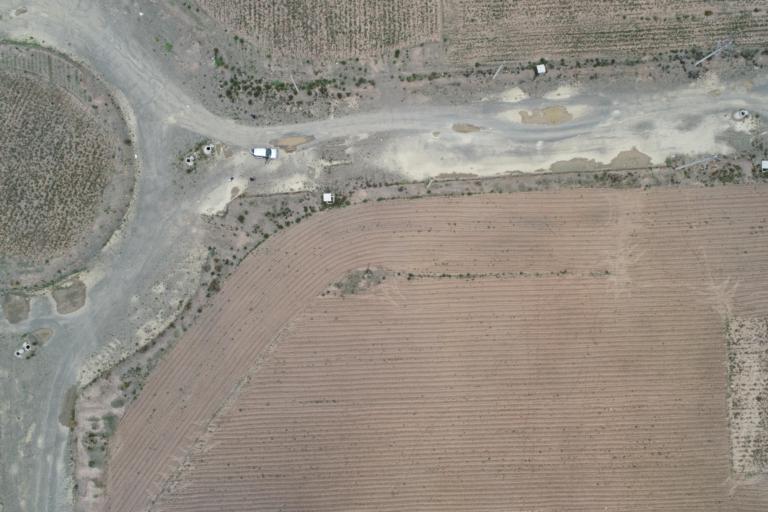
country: BO
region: La Paz
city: La Paz
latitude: -16.5149
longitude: -68.3006
